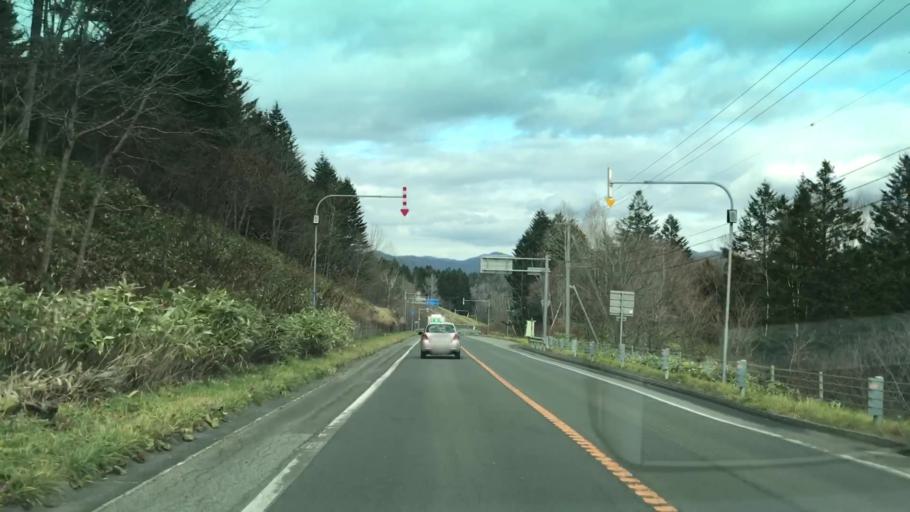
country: JP
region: Hokkaido
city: Shimo-furano
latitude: 42.9135
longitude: 142.4468
